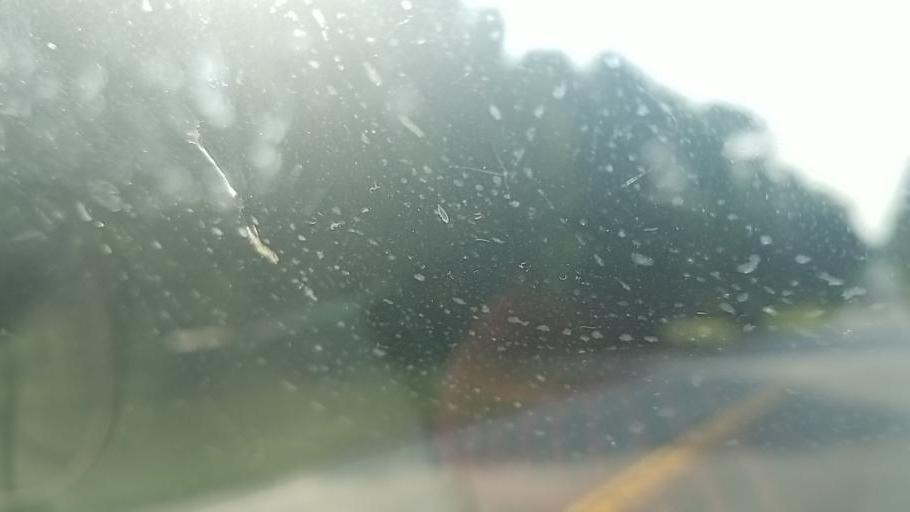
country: US
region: New York
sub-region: Fulton County
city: Broadalbin
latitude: 43.0725
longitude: -74.2545
